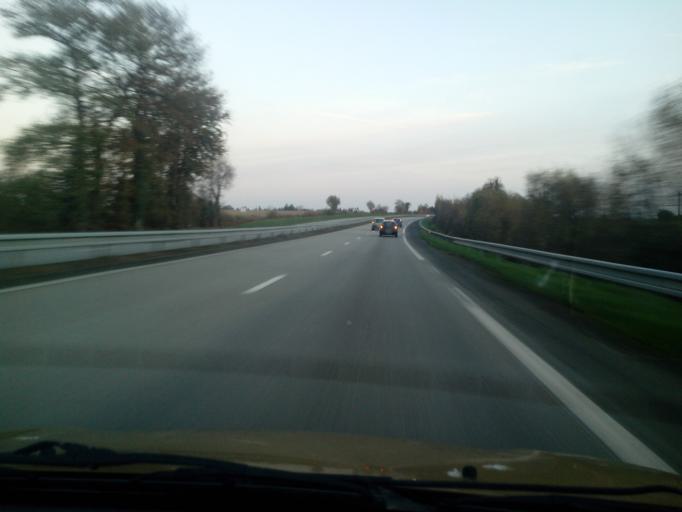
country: FR
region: Brittany
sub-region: Departement du Morbihan
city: Plumelin
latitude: 47.8953
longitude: -2.9046
